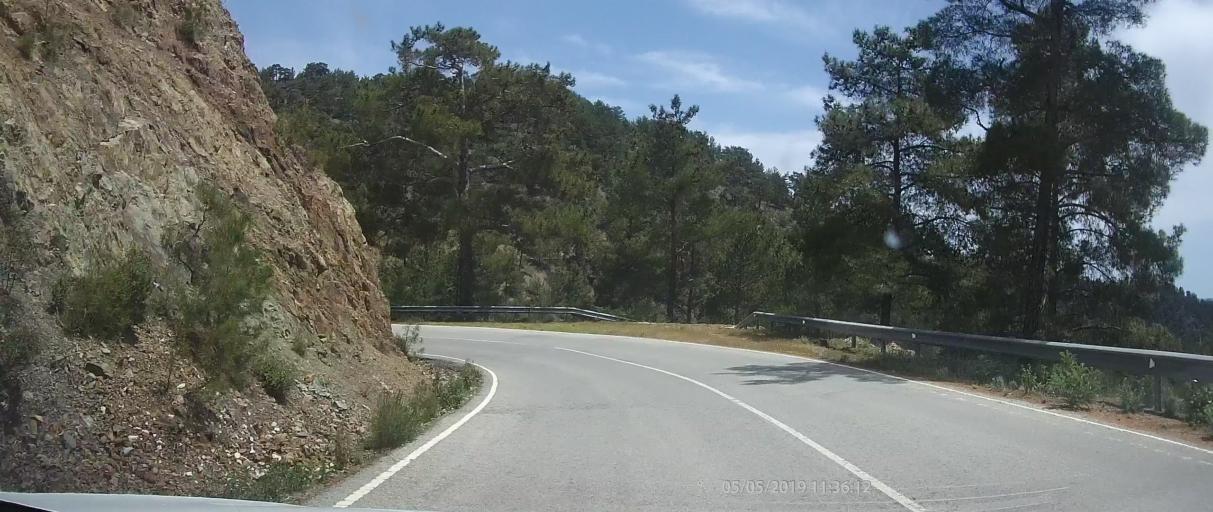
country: CY
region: Lefkosia
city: Kato Pyrgos
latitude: 34.9716
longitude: 32.6522
